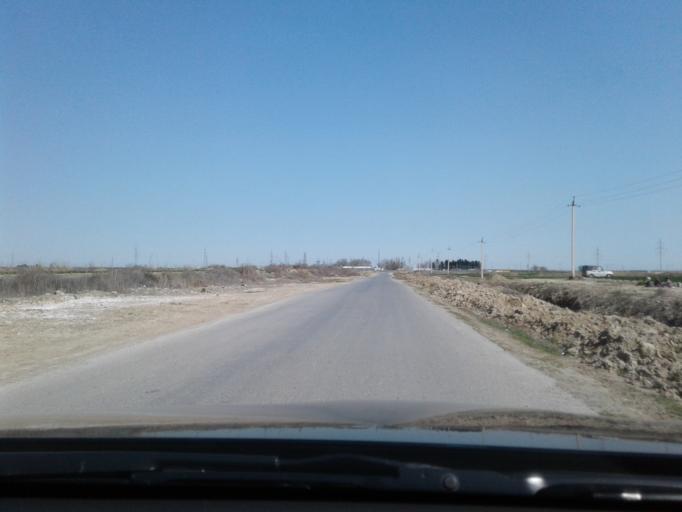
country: TM
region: Ahal
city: Abadan
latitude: 38.0990
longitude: 58.2027
